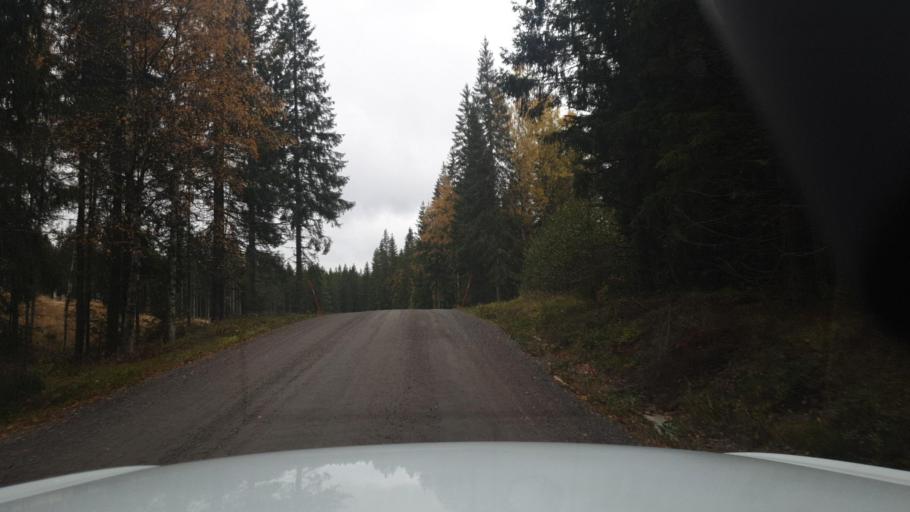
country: SE
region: Vaermland
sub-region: Sunne Kommun
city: Sunne
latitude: 59.8386
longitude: 12.9274
